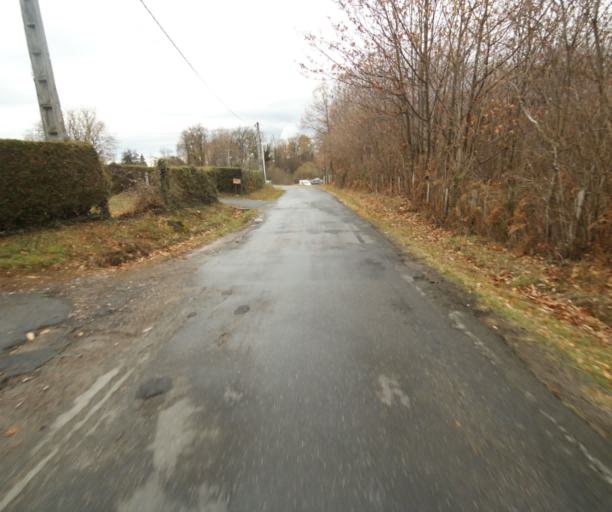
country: FR
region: Limousin
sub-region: Departement de la Correze
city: Saint-Mexant
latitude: 45.2820
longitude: 1.6421
